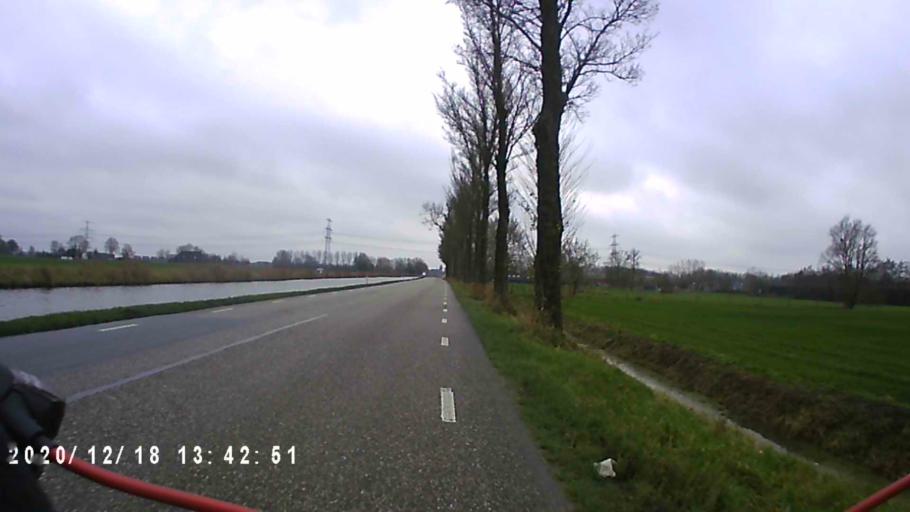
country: NL
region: Groningen
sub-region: Gemeente Bedum
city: Bedum
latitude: 53.3168
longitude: 6.5977
